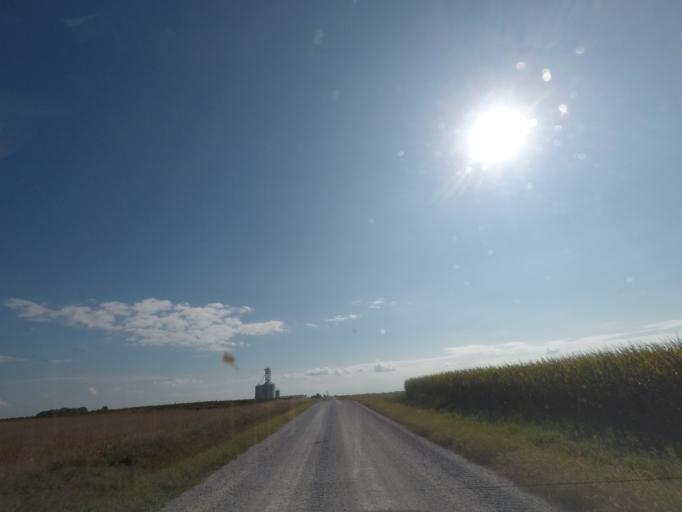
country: US
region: Iowa
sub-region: Story County
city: Nevada
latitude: 42.0490
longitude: -93.4162
